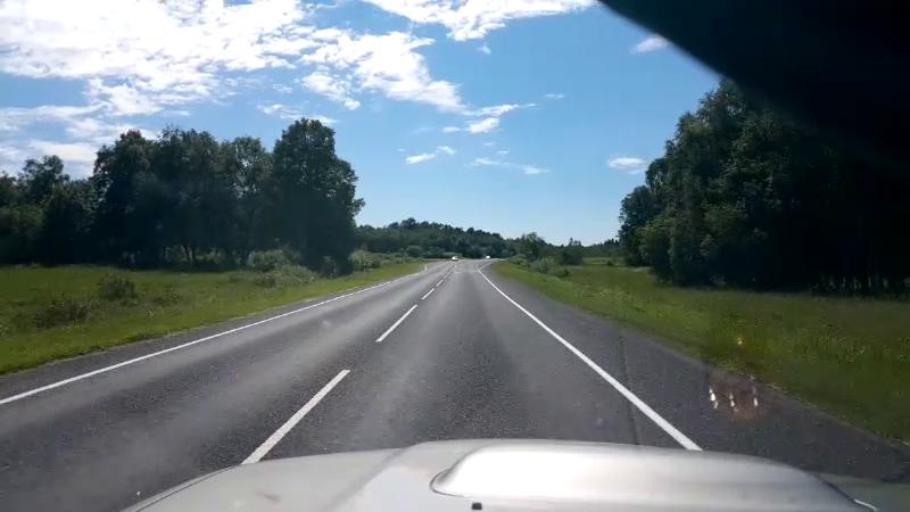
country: EE
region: Jaervamaa
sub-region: Jaerva-Jaani vald
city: Jarva-Jaani
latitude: 59.0506
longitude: 25.8817
